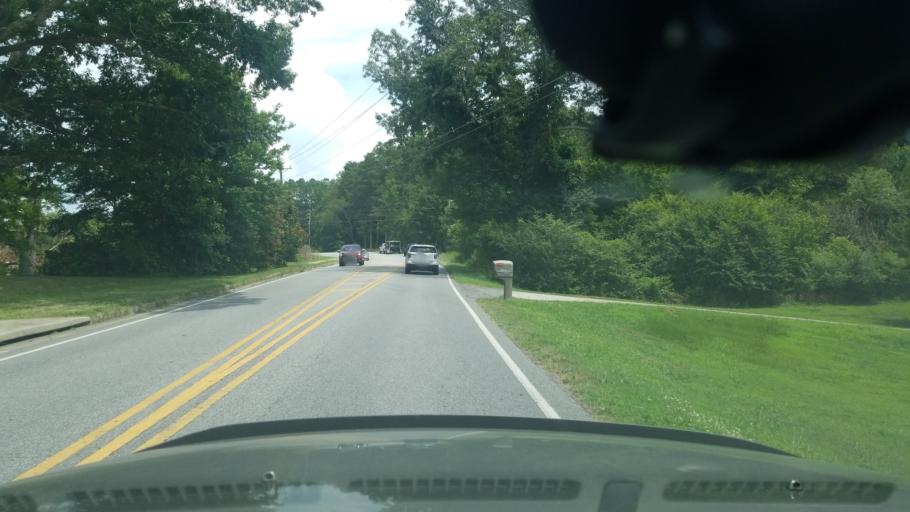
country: US
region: Georgia
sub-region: Forsyth County
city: Cumming
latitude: 34.1674
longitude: -84.1973
